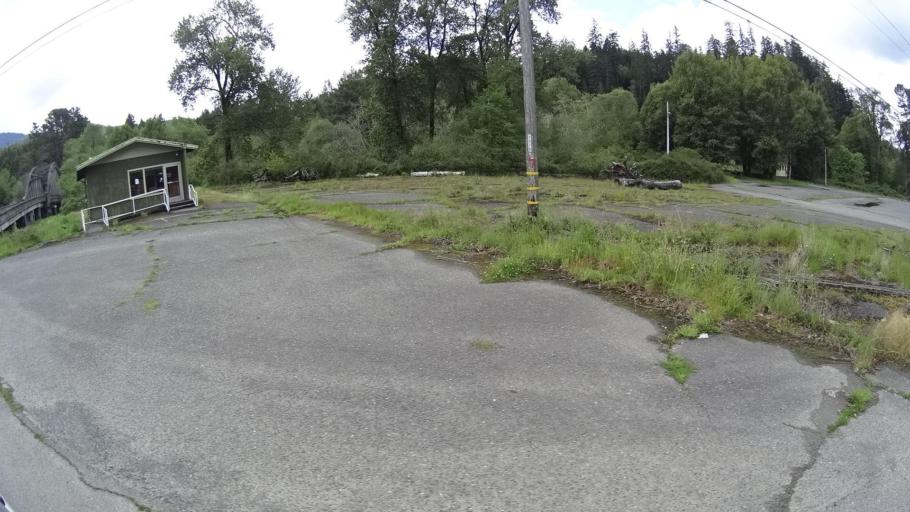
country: US
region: California
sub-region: Humboldt County
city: Blue Lake
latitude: 40.8706
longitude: -123.9626
